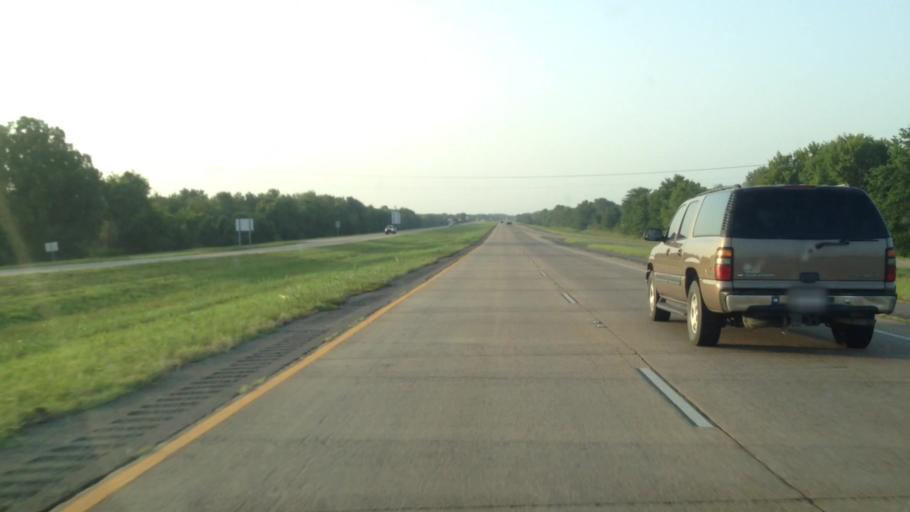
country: US
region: Louisiana
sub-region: Natchitoches Parish
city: Vienna Bend
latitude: 31.6060
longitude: -93.0468
